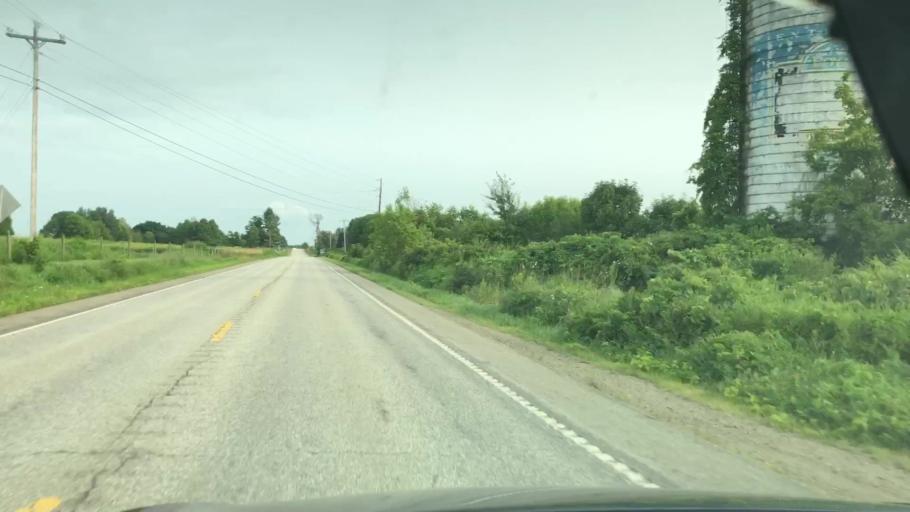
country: US
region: Pennsylvania
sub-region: Erie County
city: Union City
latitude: 41.8654
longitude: -79.8344
